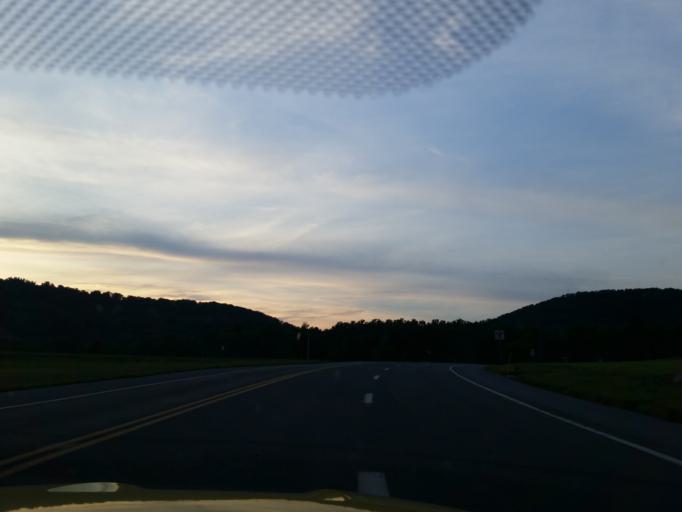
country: US
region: Pennsylvania
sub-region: Lebanon County
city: Jonestown
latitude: 40.4294
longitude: -76.5910
